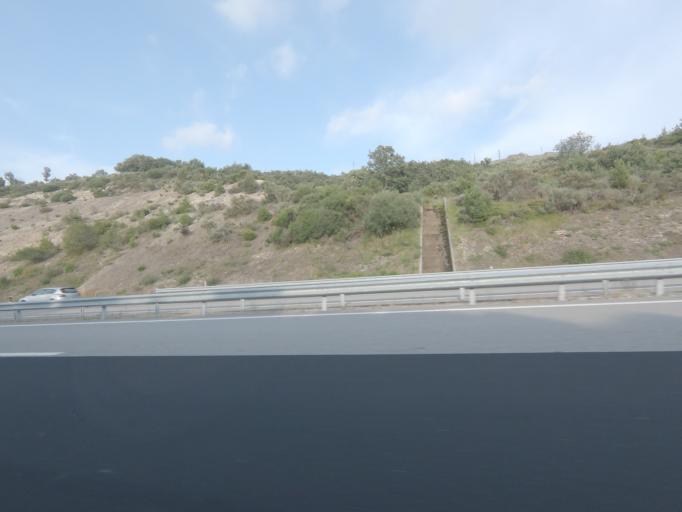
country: PT
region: Vila Real
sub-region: Vila Pouca de Aguiar
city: Vila Pouca de Aguiar
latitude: 41.4711
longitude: -7.6442
